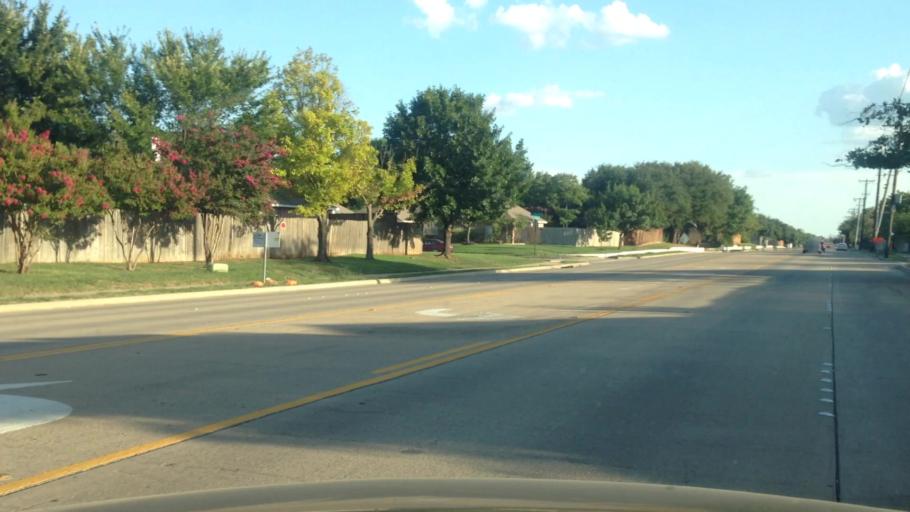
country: US
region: Texas
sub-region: Tarrant County
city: Watauga
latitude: 32.8870
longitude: -97.2378
